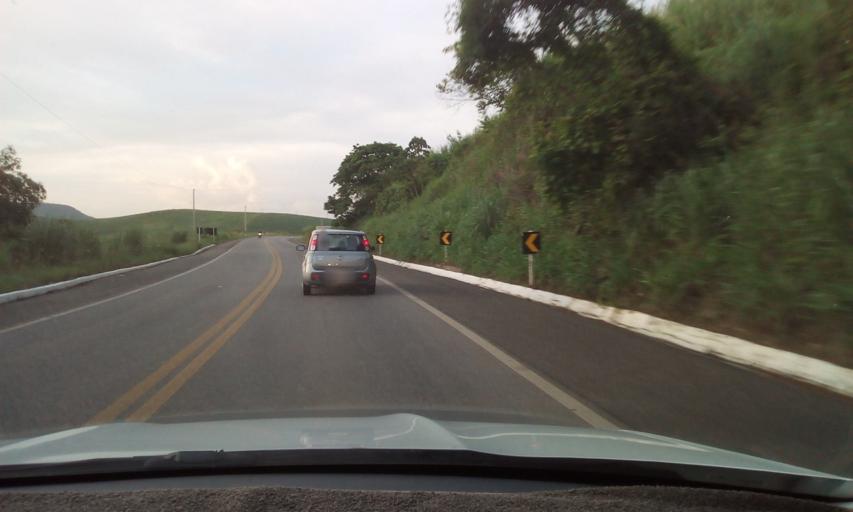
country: BR
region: Pernambuco
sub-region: Vicencia
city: Vicencia
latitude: -7.6222
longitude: -35.2411
